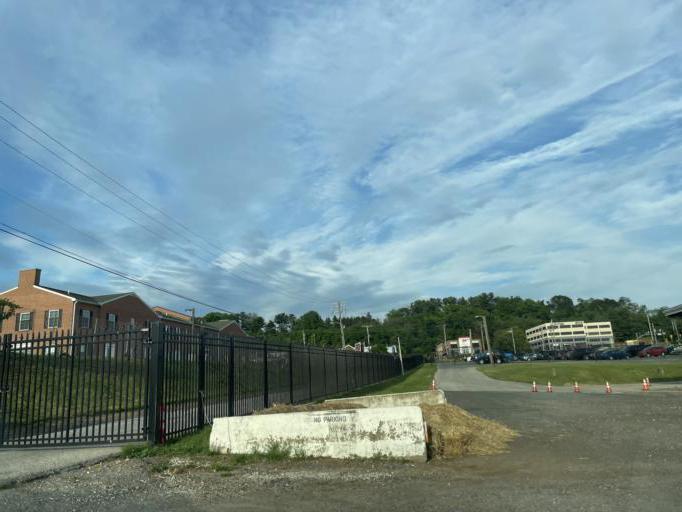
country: US
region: Maryland
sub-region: Baltimore County
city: Timonium
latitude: 39.4487
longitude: -76.6321
